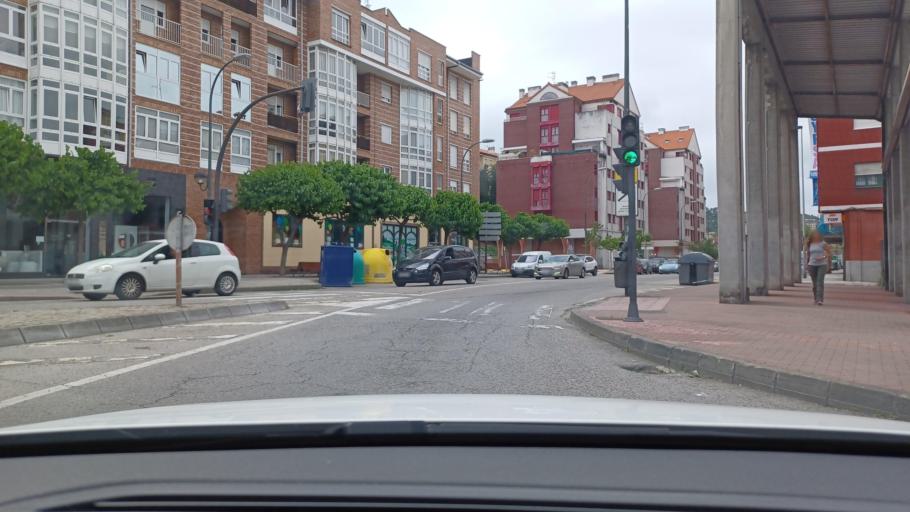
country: ES
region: Asturias
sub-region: Province of Asturias
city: Aviles
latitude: 43.5628
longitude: -5.9242
